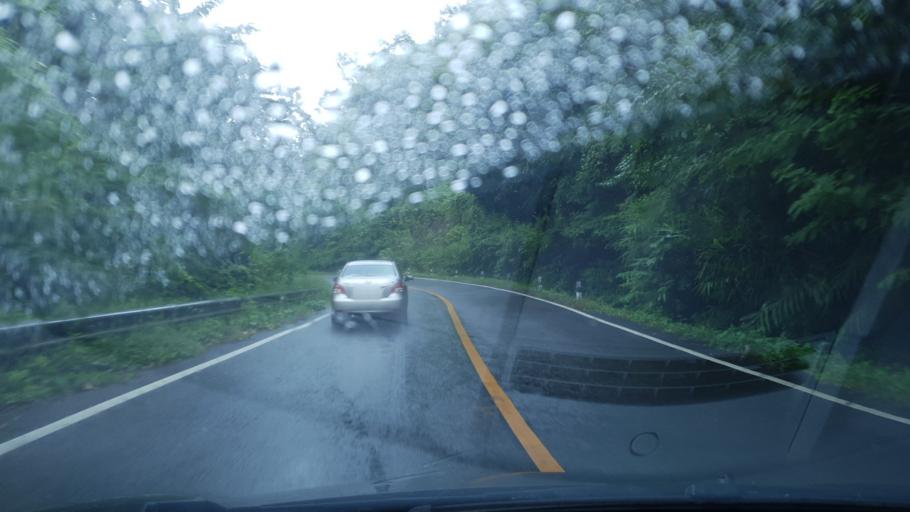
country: TH
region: Mae Hong Son
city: Khun Yuam
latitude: 18.6711
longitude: 97.9269
